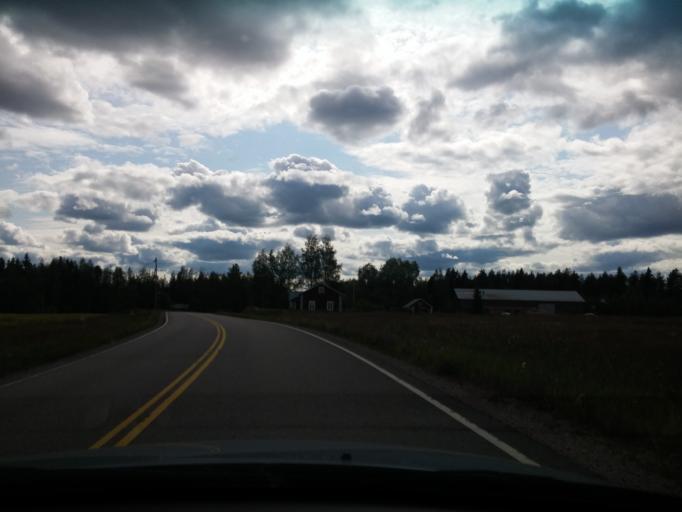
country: FI
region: Central Finland
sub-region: Saarijaervi-Viitasaari
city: Pylkoenmaeki
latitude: 62.6261
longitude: 24.7847
